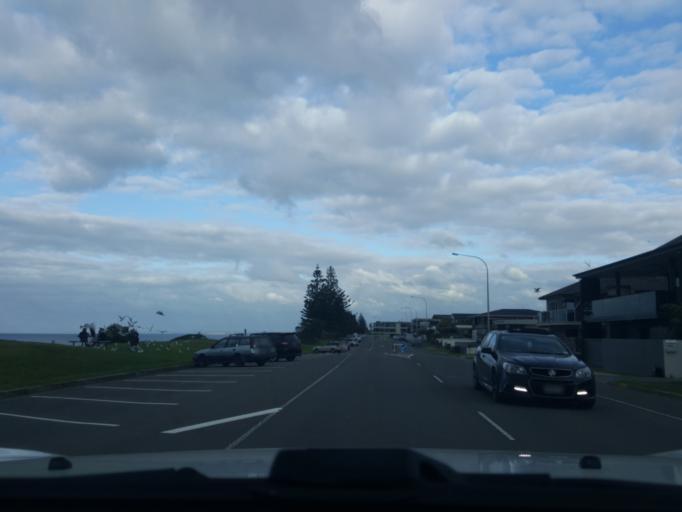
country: NZ
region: Bay of Plenty
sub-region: Tauranga City
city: Tauranga
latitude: -37.6476
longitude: 176.1994
